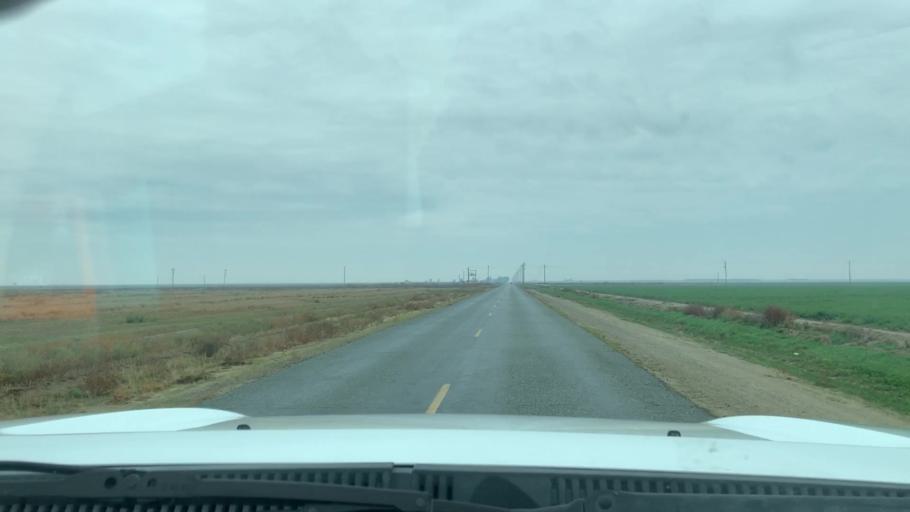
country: US
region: California
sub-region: Tulare County
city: Alpaugh
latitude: 35.7610
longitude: -119.4417
